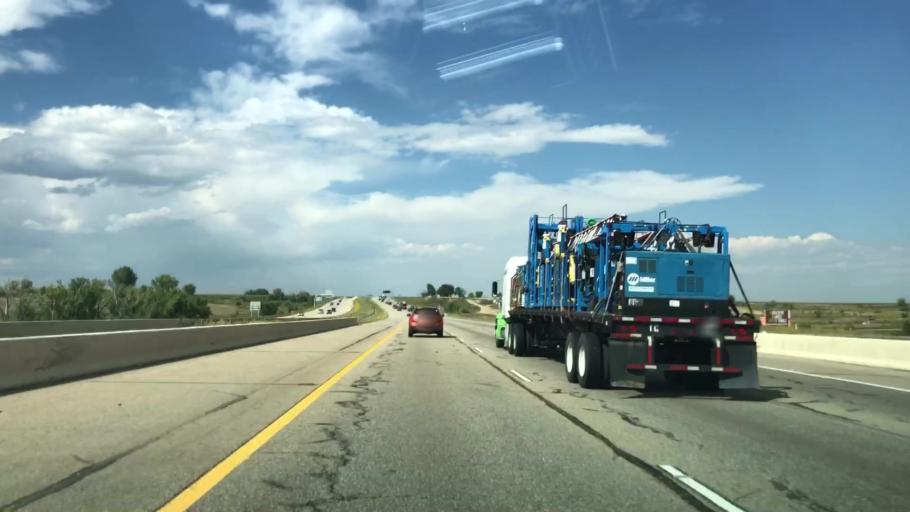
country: US
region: Colorado
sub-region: Weld County
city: Mead
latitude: 40.1757
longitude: -104.9775
